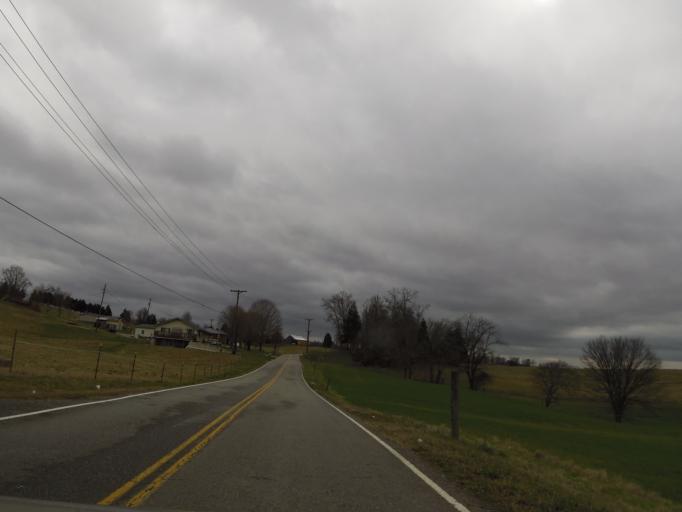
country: US
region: Tennessee
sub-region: Grainger County
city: Rutledge
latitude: 36.1968
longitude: -83.5443
